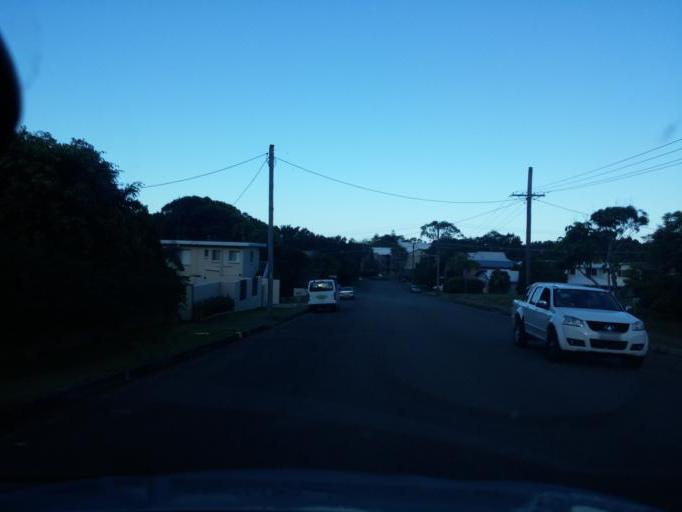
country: AU
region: New South Wales
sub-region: Port Macquarie-Hastings
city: Port Macquarie
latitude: -31.4442
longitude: 152.9215
